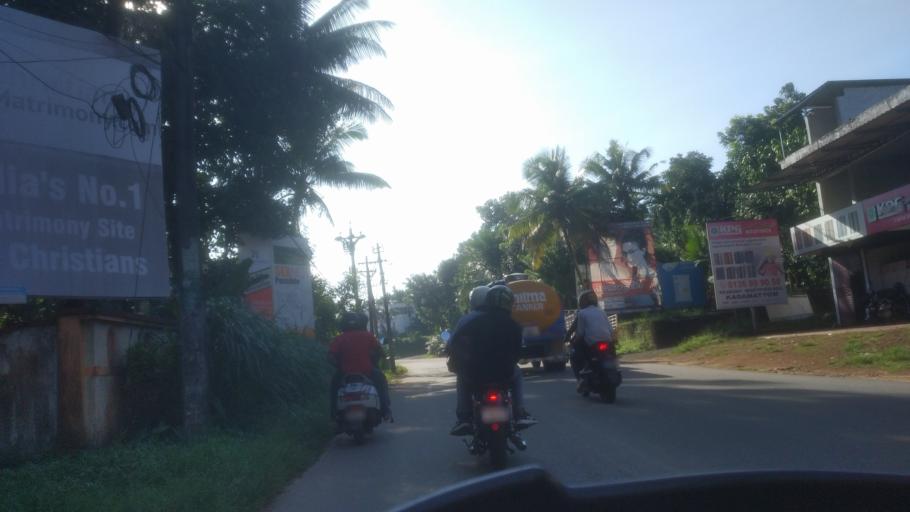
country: IN
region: Kerala
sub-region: Ernakulam
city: Ramamangalam
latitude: 9.9745
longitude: 76.5019
